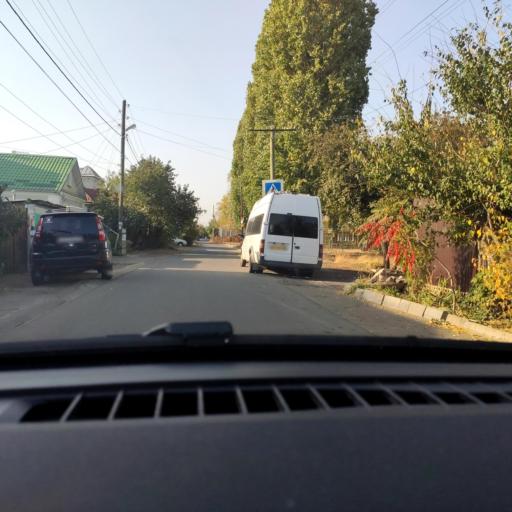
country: RU
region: Voronezj
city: Voronezh
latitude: 51.6265
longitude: 39.1746
